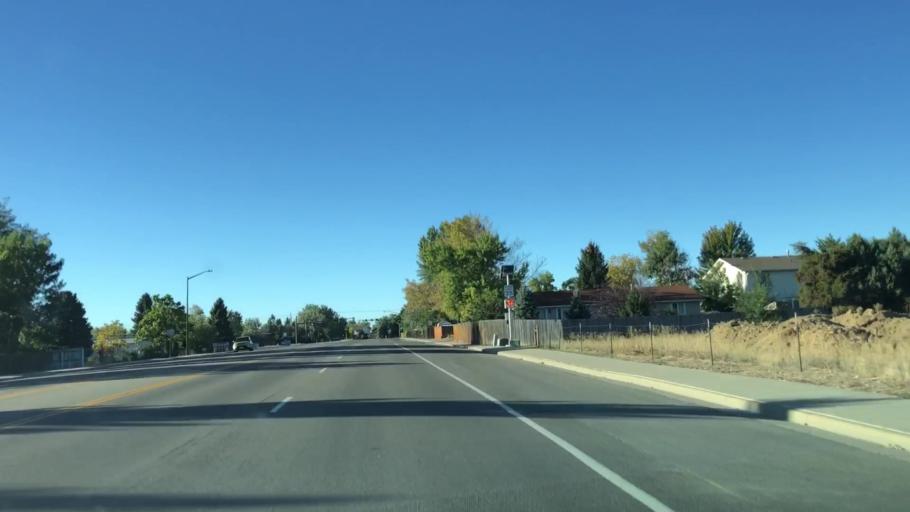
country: US
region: Colorado
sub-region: Larimer County
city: Loveland
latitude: 40.3808
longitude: -105.1160
